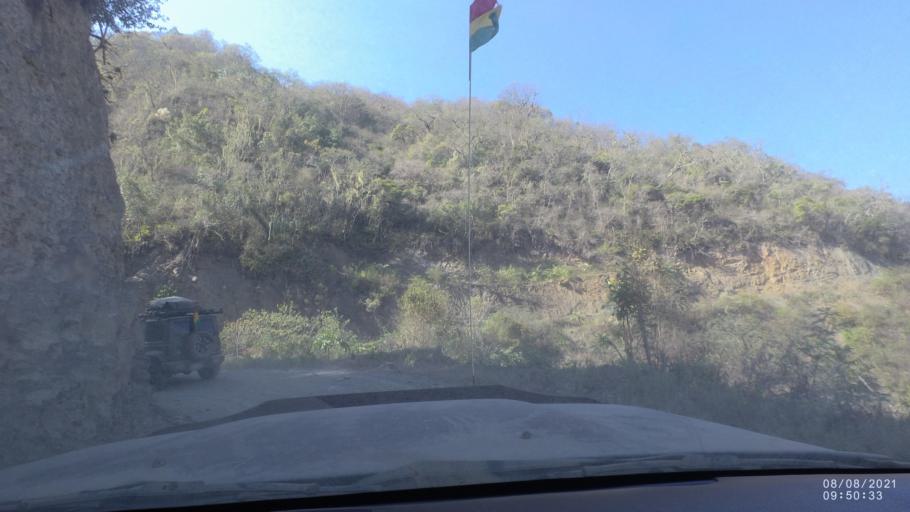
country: BO
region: La Paz
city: Quime
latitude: -16.6211
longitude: -66.7281
